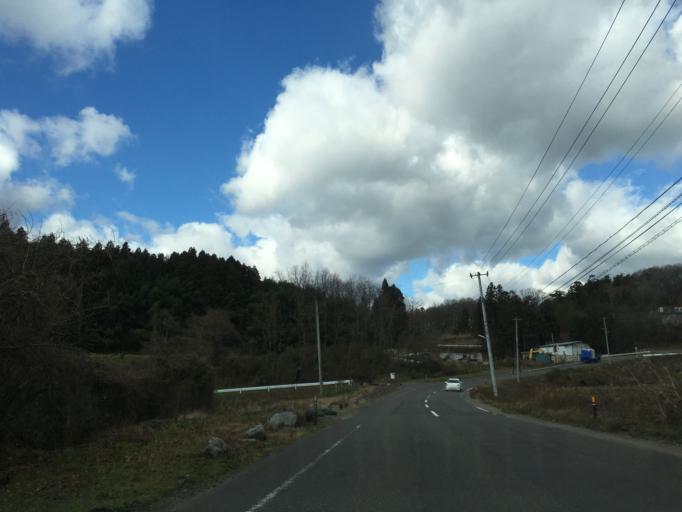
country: JP
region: Fukushima
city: Sukagawa
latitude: 37.3301
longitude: 140.4402
